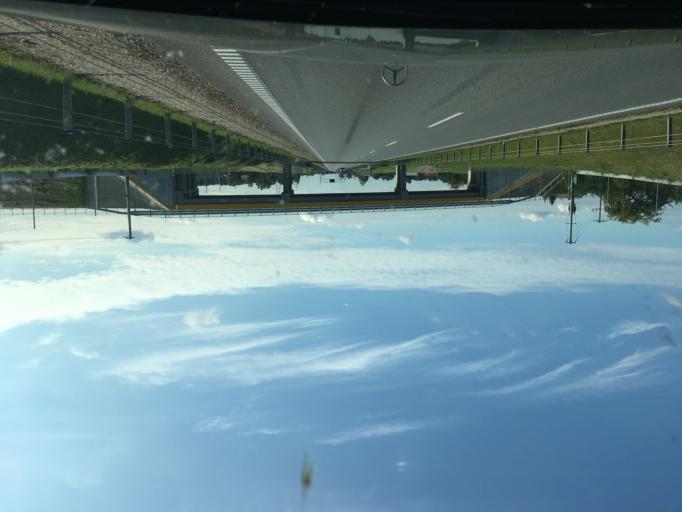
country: PL
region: Podlasie
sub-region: Powiat augustowski
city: Augustow
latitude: 53.8822
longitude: 22.8749
